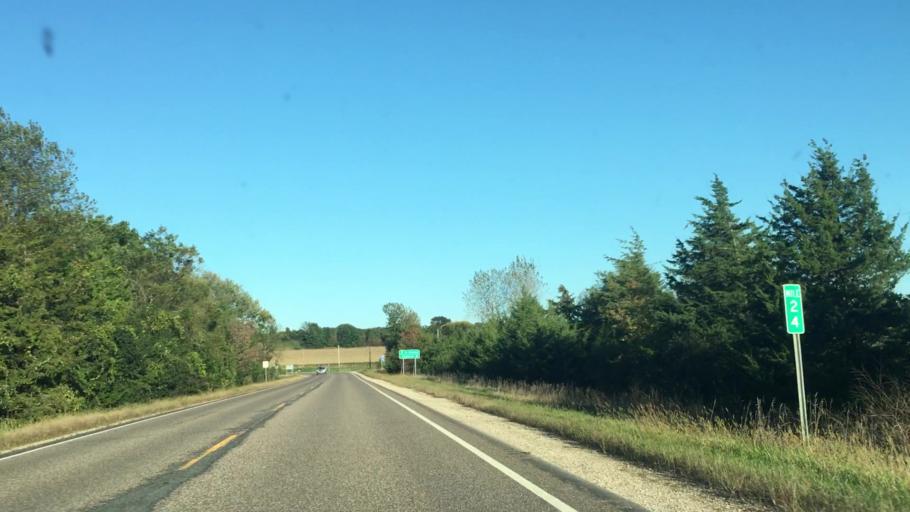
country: US
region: Minnesota
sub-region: Fillmore County
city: Chatfield
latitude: 43.8543
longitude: -92.1135
